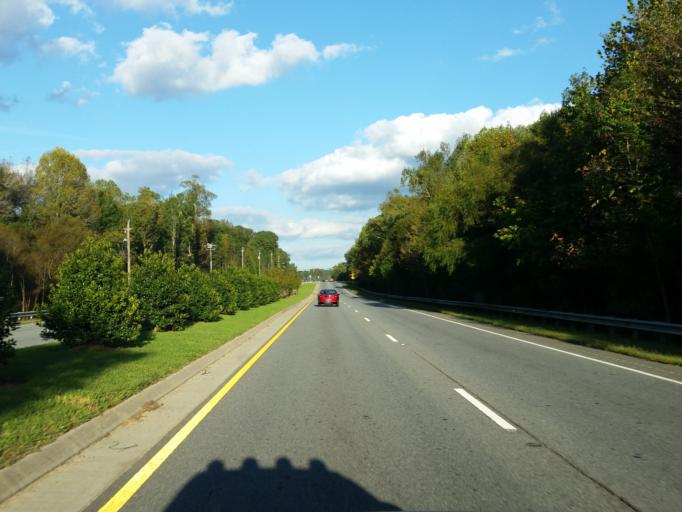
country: US
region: Georgia
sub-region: Cobb County
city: Powder Springs
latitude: 33.8978
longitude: -84.6388
